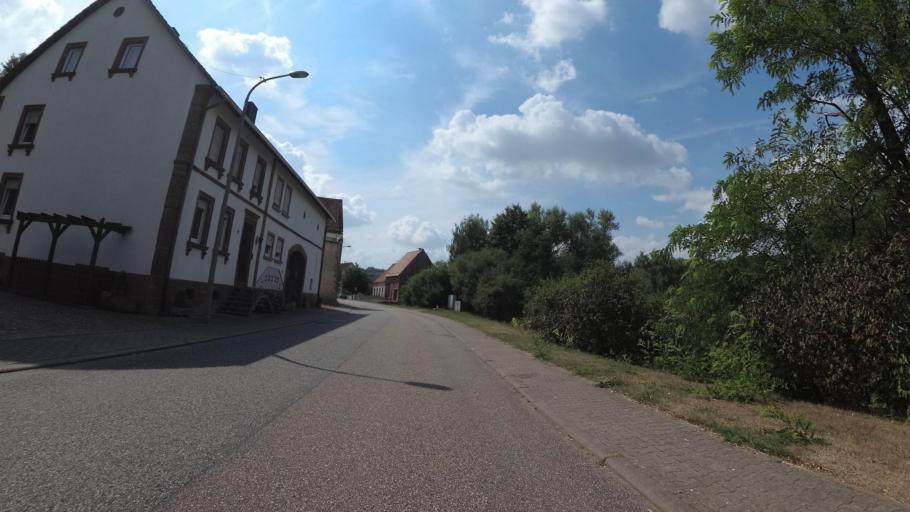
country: DE
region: Rheinland-Pfalz
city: Dietrichingen
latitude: 49.1920
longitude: 7.4140
